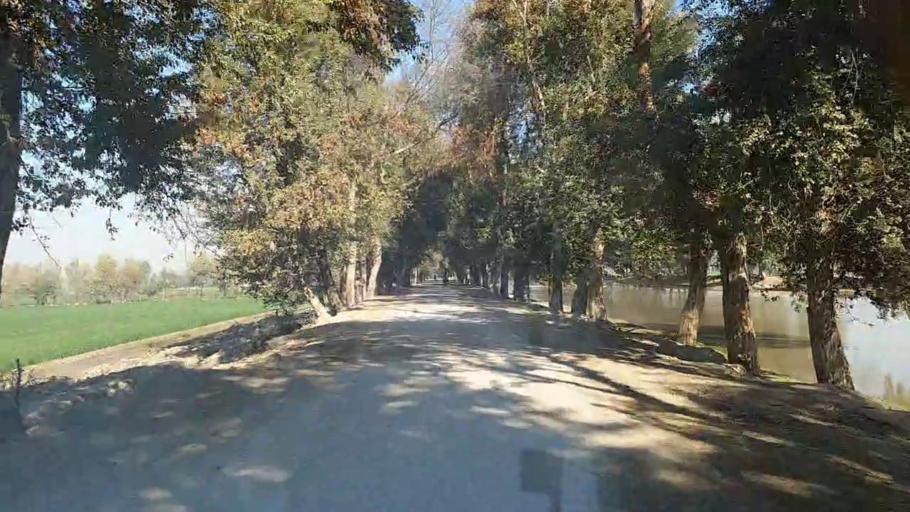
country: PK
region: Sindh
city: Khairpur
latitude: 27.9987
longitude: 69.6524
